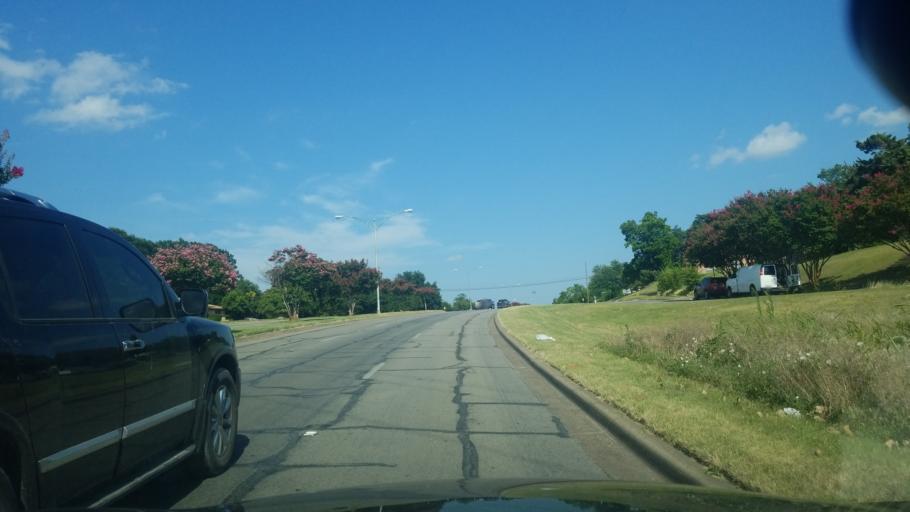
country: US
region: Texas
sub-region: Dallas County
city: Dallas
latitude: 32.7196
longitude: -96.7920
